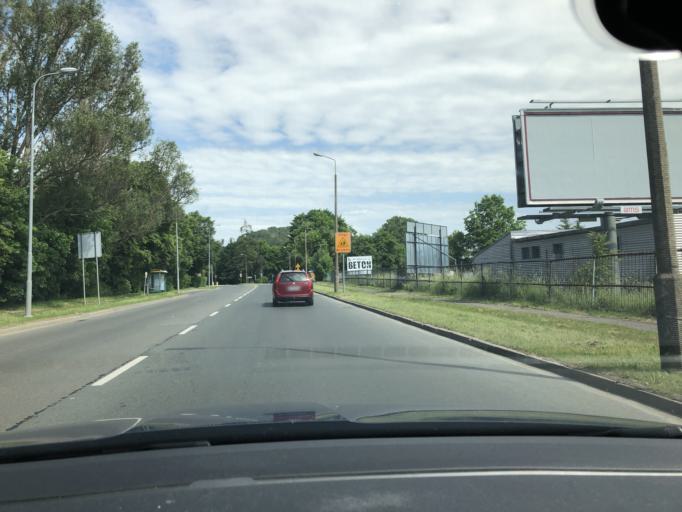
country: PL
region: Lower Silesian Voivodeship
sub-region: Powiat jeleniogorski
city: Jezow Sudecki
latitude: 50.9020
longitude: 15.7837
